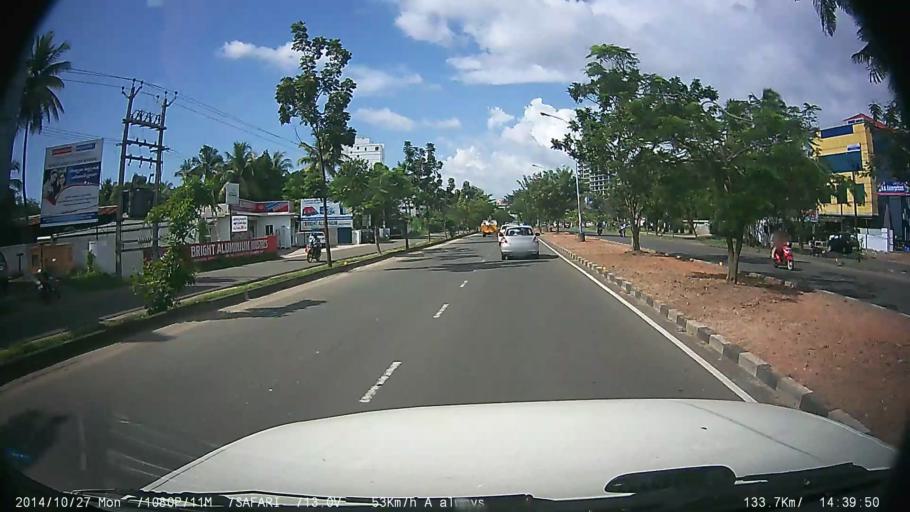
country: IN
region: Kerala
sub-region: Ernakulam
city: Cochin
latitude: 9.9929
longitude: 76.3150
